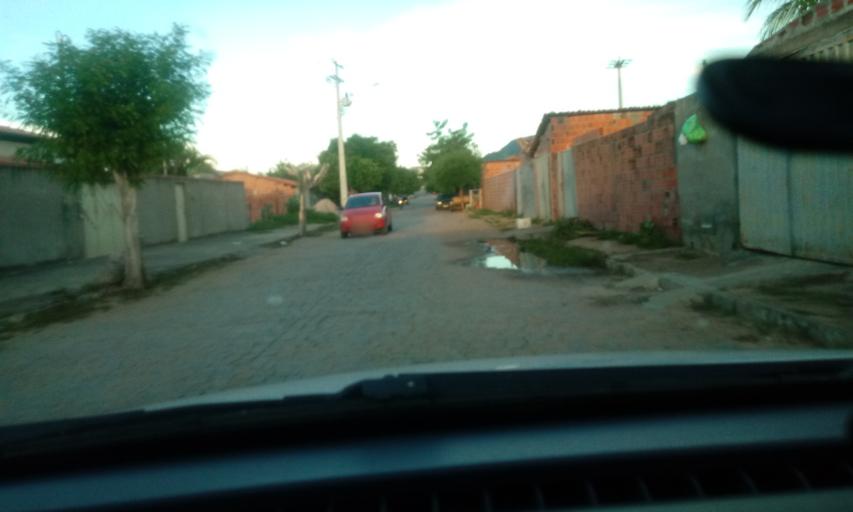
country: BR
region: Bahia
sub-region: Riacho De Santana
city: Riacho de Santana
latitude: -13.9090
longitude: -42.8477
